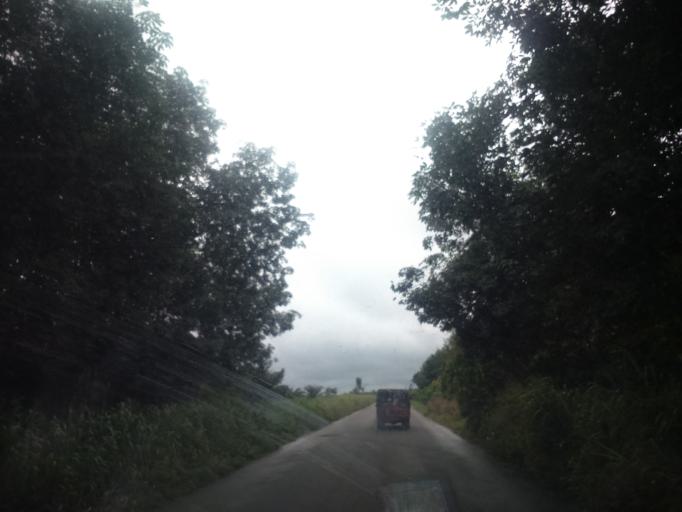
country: CI
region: Sud-Comoe
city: Bonoua
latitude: 5.2851
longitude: -3.4682
